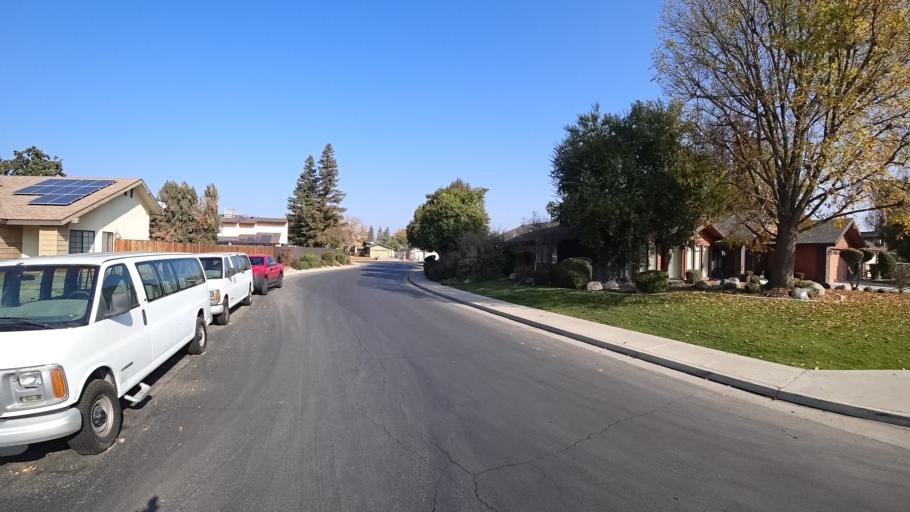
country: US
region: California
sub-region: Kern County
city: Greenacres
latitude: 35.3332
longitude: -119.0832
